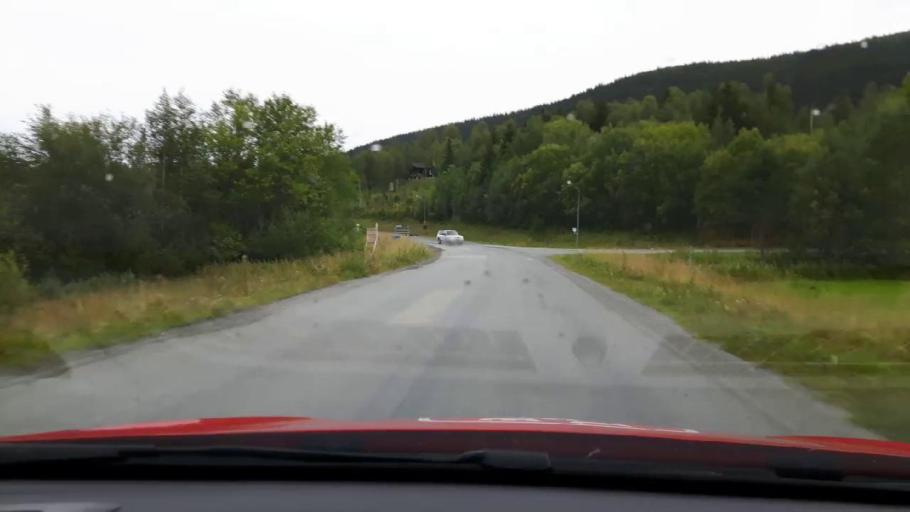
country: SE
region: Jaemtland
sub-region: Are Kommun
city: Are
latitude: 63.4896
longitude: 13.1272
